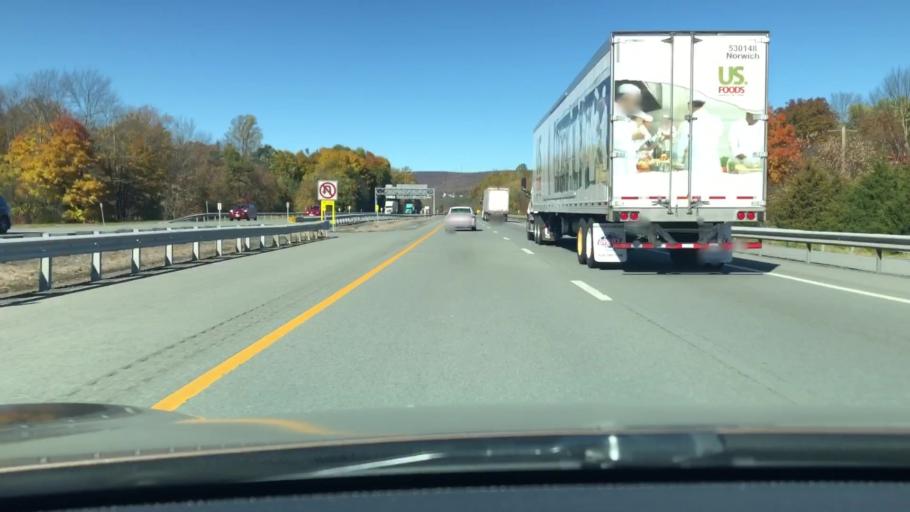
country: US
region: New York
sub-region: Orange County
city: Central Valley
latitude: 41.3314
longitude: -74.1137
